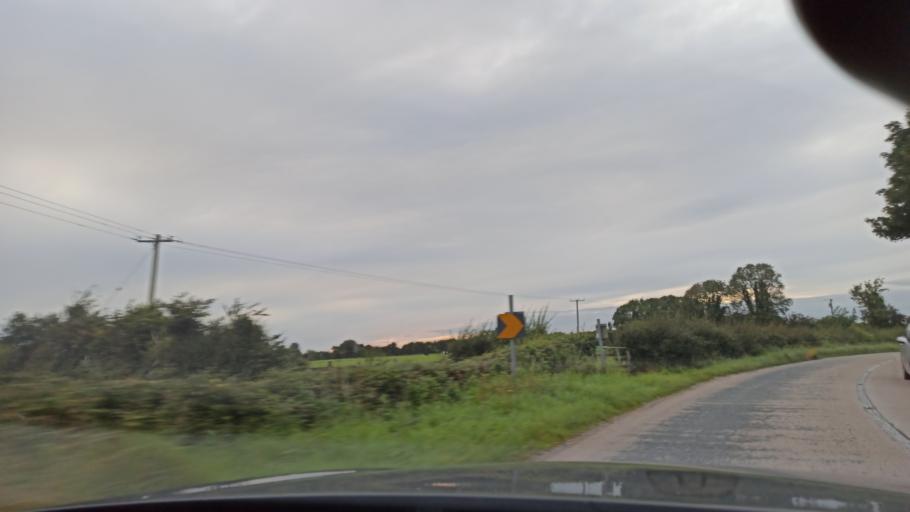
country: IE
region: Munster
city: Cashel
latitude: 52.4783
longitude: -7.8516
